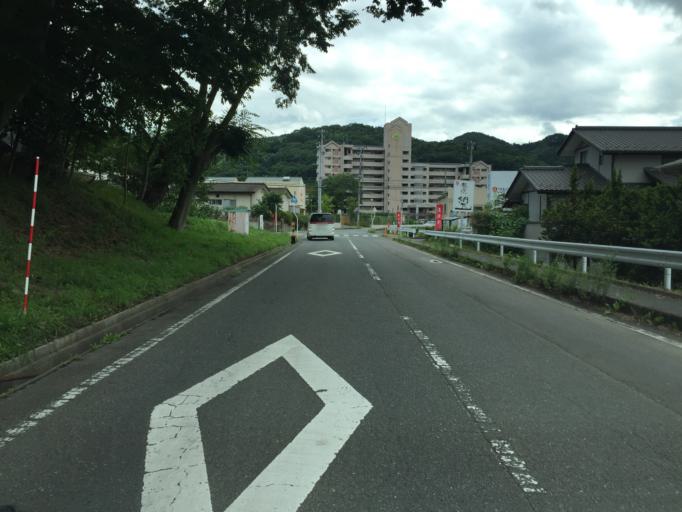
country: JP
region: Fukushima
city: Fukushima-shi
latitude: 37.7449
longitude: 140.4863
